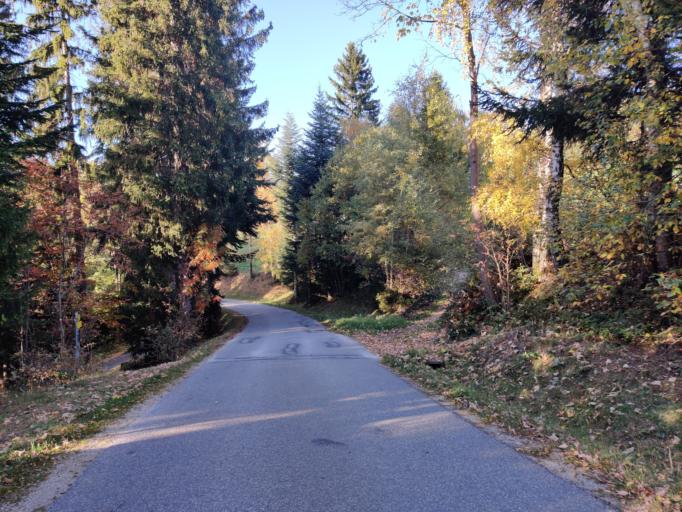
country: AT
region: Styria
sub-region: Politischer Bezirk Hartberg-Fuerstenfeld
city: Sankt Jakob im Walde
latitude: 47.4684
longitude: 15.8004
